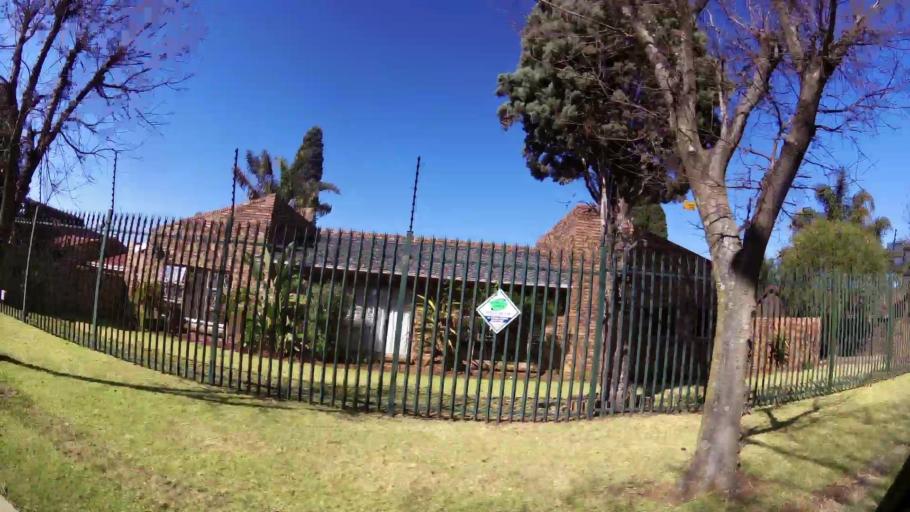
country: ZA
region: Gauteng
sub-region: Ekurhuleni Metropolitan Municipality
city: Germiston
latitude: -26.2998
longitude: 28.1015
